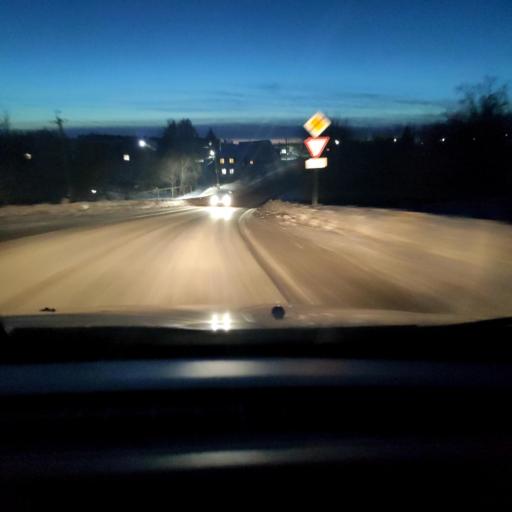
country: RU
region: Samara
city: Kinel'
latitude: 53.2683
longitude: 50.5912
